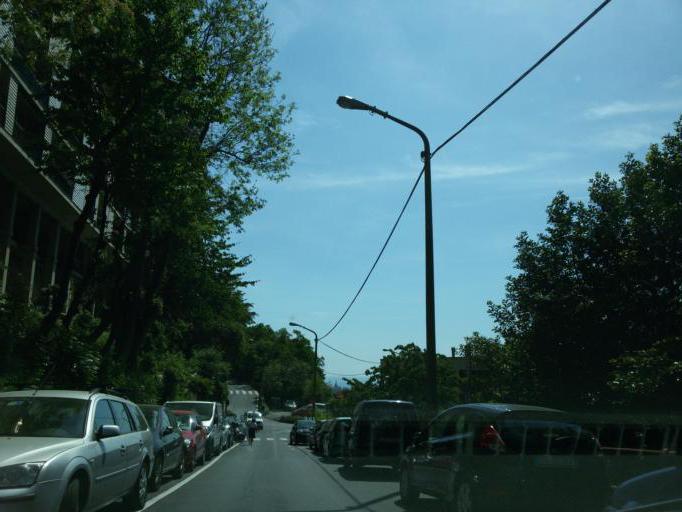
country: IT
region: Liguria
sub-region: Provincia di Genova
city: Genoa
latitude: 44.4237
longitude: 8.9612
